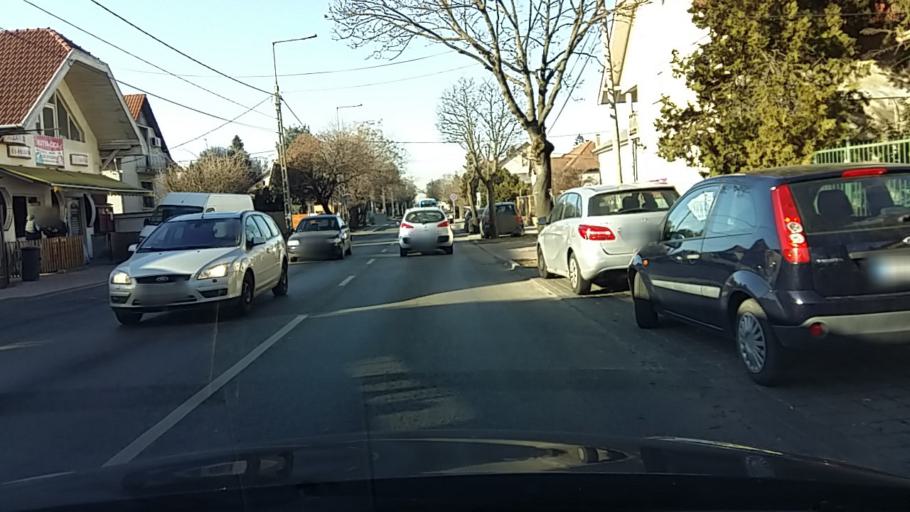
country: HU
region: Budapest
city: Budapest XVI. keruelet
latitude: 47.5233
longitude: 19.1718
